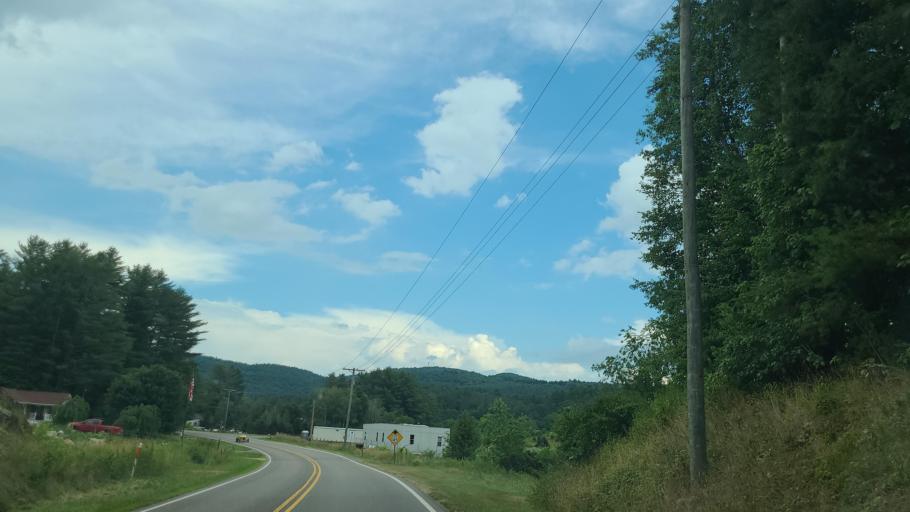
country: US
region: North Carolina
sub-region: Alleghany County
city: Sparta
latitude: 36.3954
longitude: -81.2508
